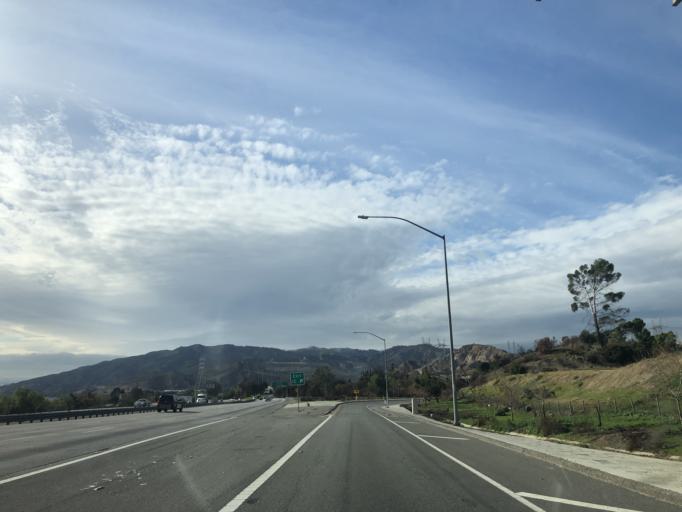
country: US
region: California
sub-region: Los Angeles County
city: San Fernando
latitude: 34.3234
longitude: -118.4758
